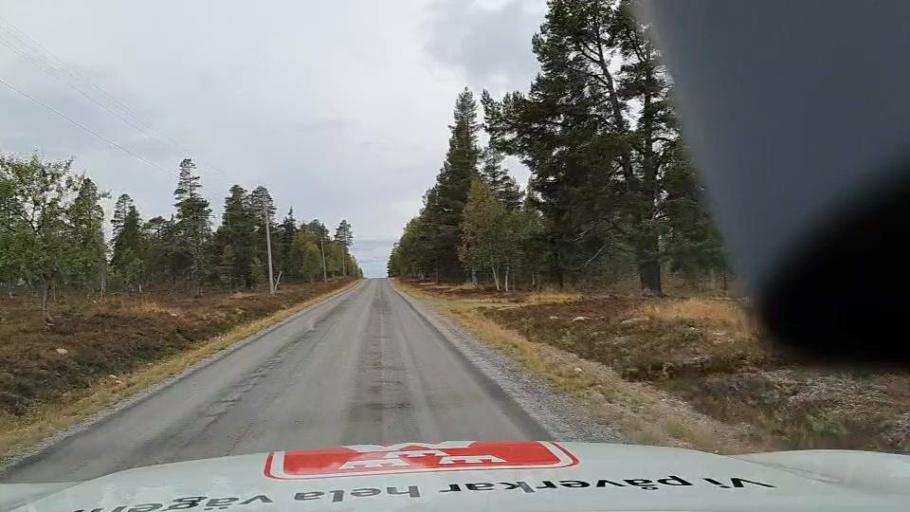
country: NO
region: Hedmark
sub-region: Engerdal
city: Engerdal
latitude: 62.0938
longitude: 12.8172
